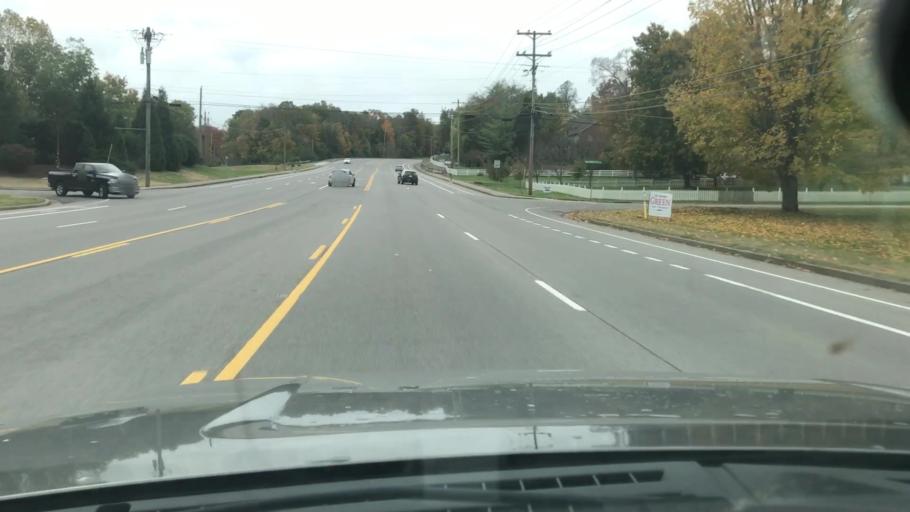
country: US
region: Tennessee
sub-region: Williamson County
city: Franklin
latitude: 35.9740
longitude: -86.8863
